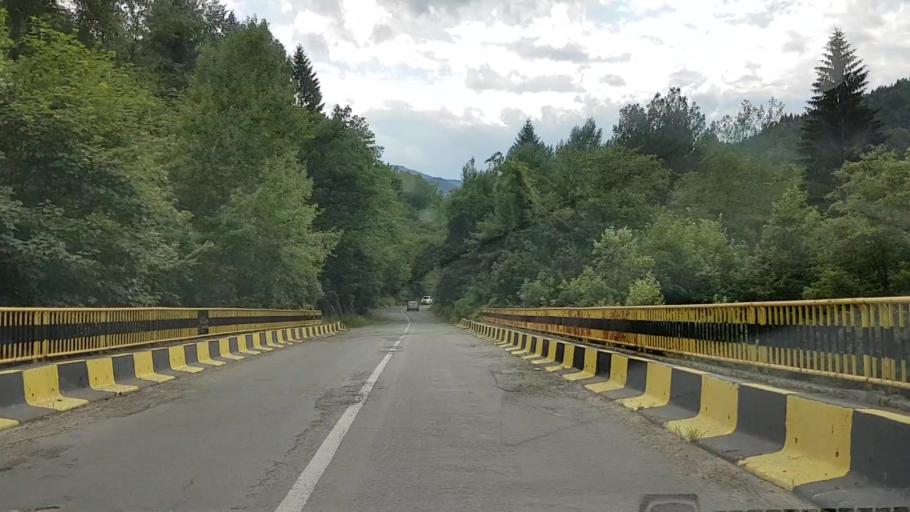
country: RO
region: Neamt
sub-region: Comuna Bicaz
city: Dodeni
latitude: 46.9383
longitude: 26.1108
